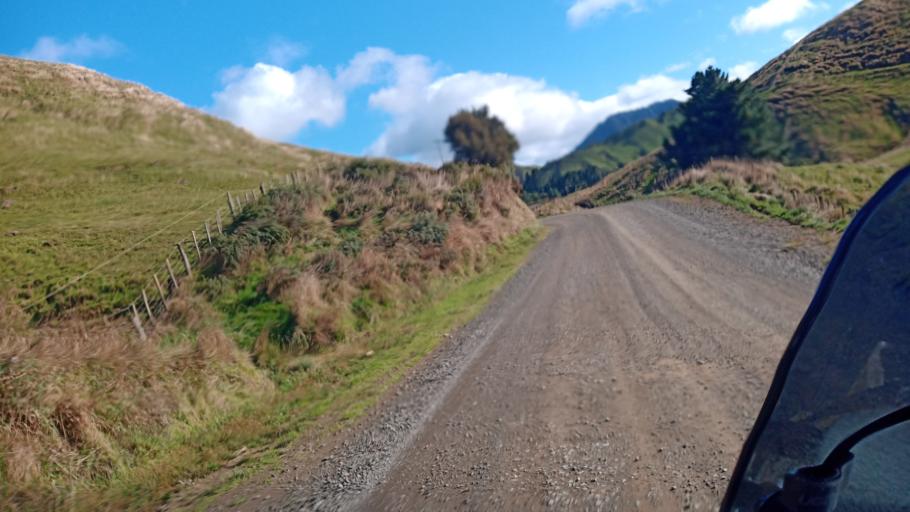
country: NZ
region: Bay of Plenty
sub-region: Opotiki District
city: Opotiki
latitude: -38.4687
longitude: 177.4297
